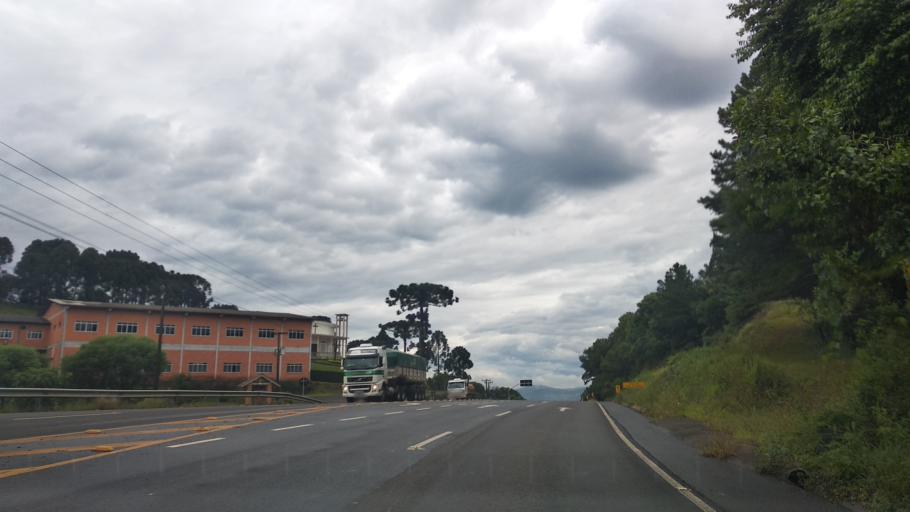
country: BR
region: Santa Catarina
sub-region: Videira
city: Videira
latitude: -27.0776
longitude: -51.2339
